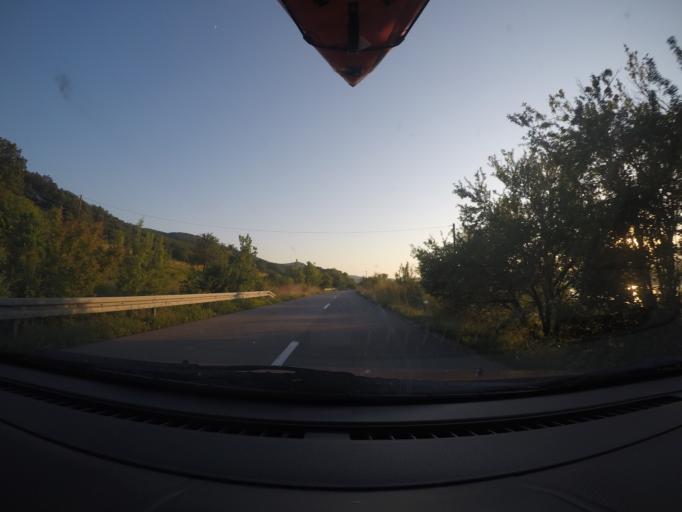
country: RO
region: Mehedinti
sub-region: Comuna Eselnita
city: Eselnita
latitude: 44.6761
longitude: 22.3960
